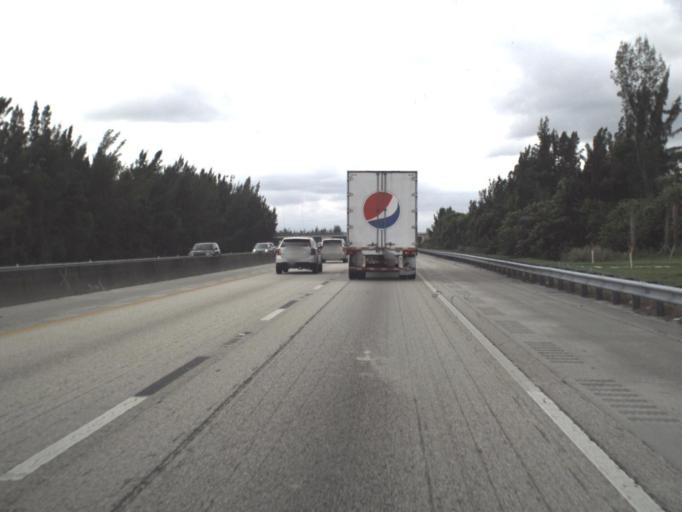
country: US
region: Florida
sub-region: Palm Beach County
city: Schall Circle
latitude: 26.7668
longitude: -80.1336
